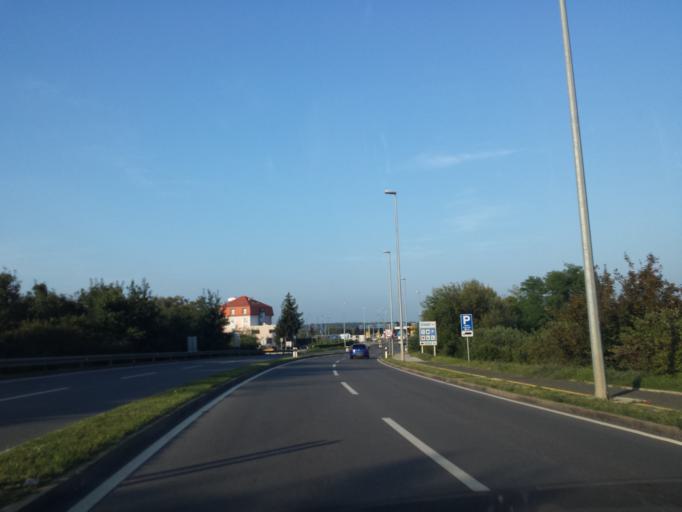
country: HR
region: Karlovacka
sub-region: Grad Karlovac
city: Karlovac
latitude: 45.5103
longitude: 15.5447
